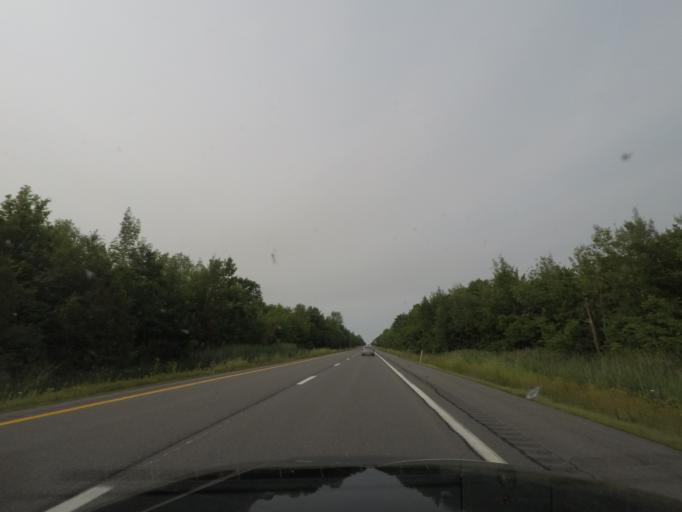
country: US
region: New York
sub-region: Clinton County
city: Champlain
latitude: 44.9483
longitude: -73.4480
